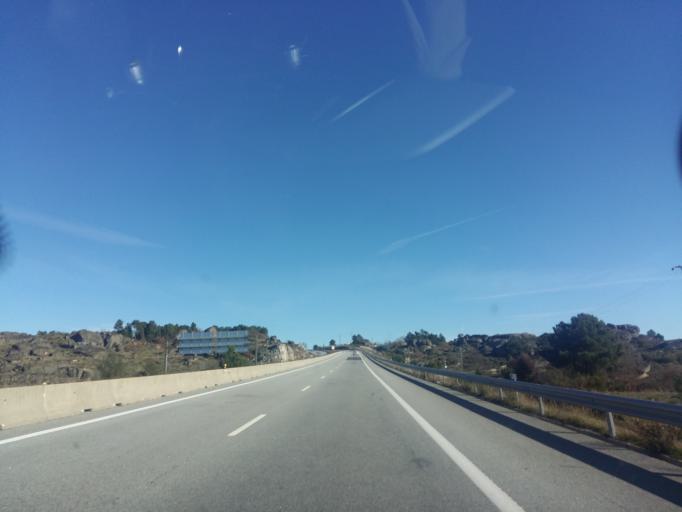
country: PT
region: Guarda
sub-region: Guarda
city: Sequeira
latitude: 40.5767
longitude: -7.1877
